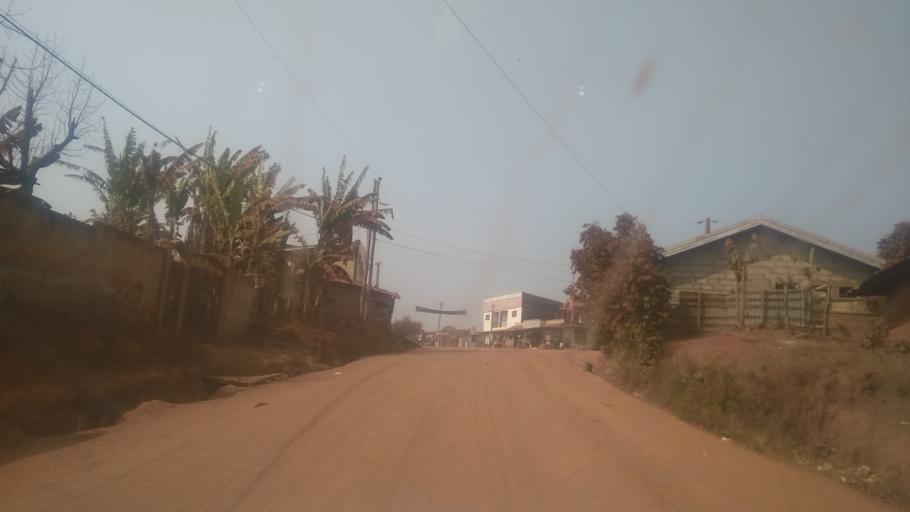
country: CM
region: West
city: Bafoussam
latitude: 5.5110
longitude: 10.4038
